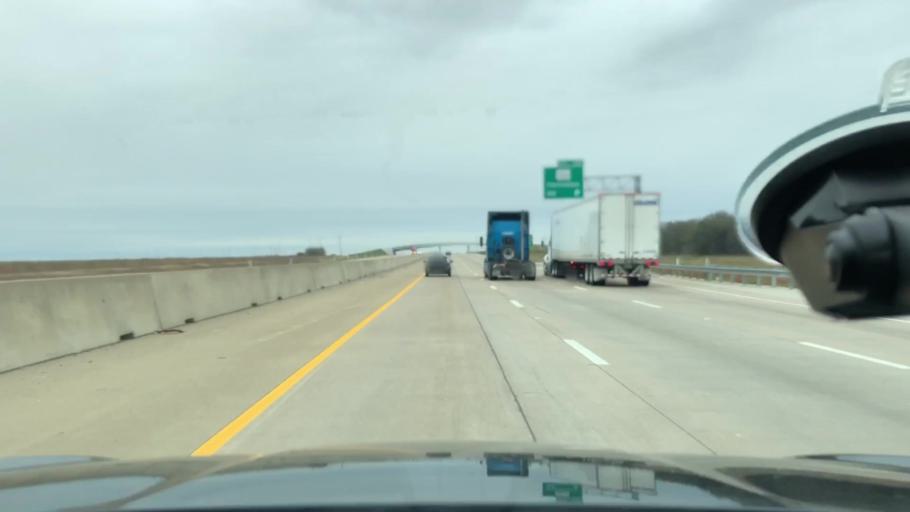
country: US
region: Texas
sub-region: Ellis County
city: Nash
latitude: 32.2545
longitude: -96.8739
